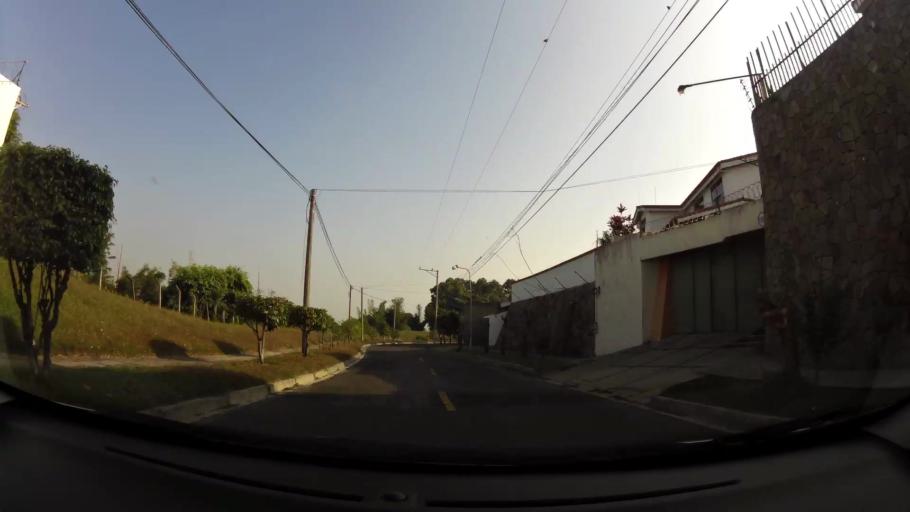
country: SV
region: La Libertad
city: Antiguo Cuscatlan
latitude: 13.6795
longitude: -89.2217
